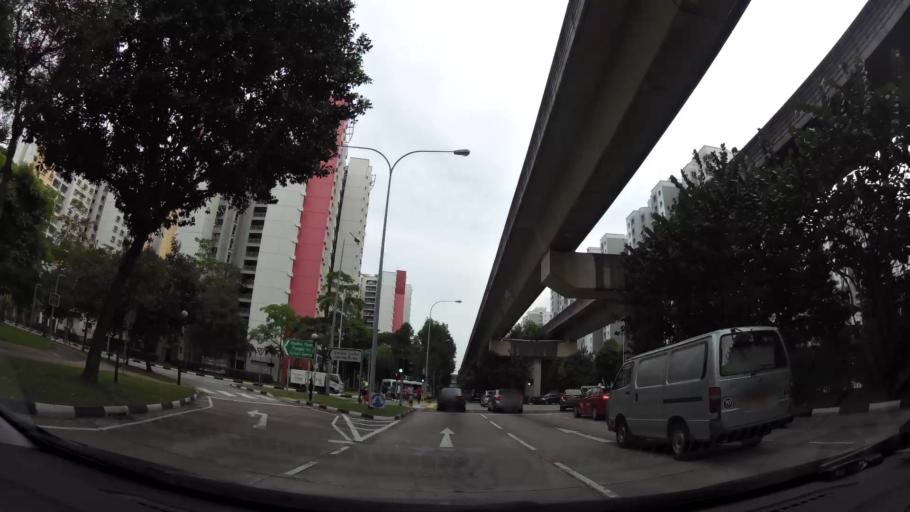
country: MY
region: Johor
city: Kampung Pasir Gudang Baru
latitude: 1.3957
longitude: 103.9108
